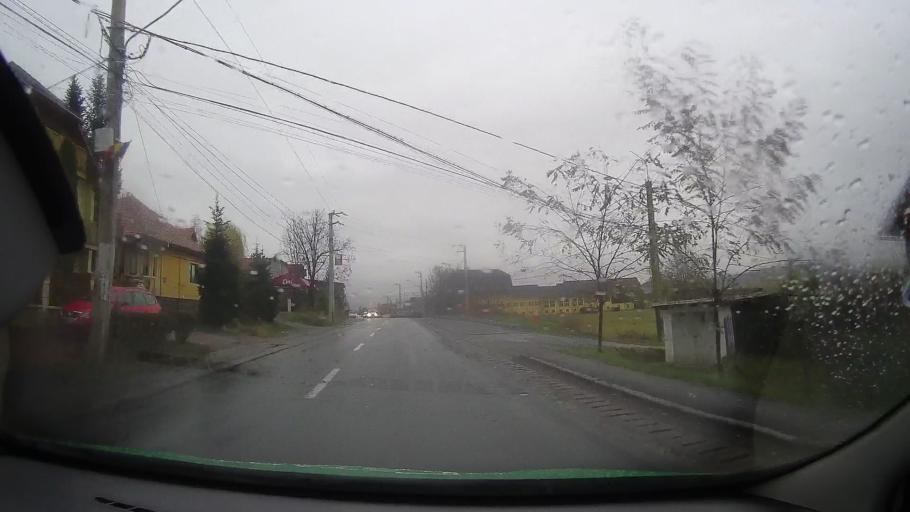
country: RO
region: Mures
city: Reghin-Sat
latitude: 46.7923
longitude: 24.7149
